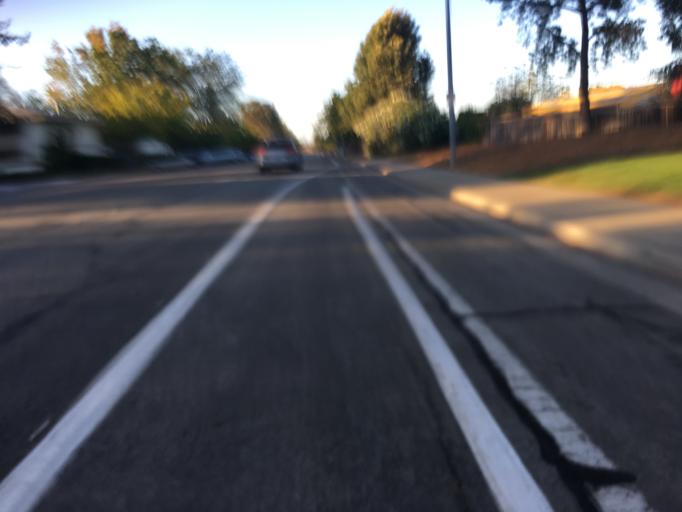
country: US
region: California
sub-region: Santa Clara County
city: Cupertino
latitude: 37.3276
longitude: -122.0504
